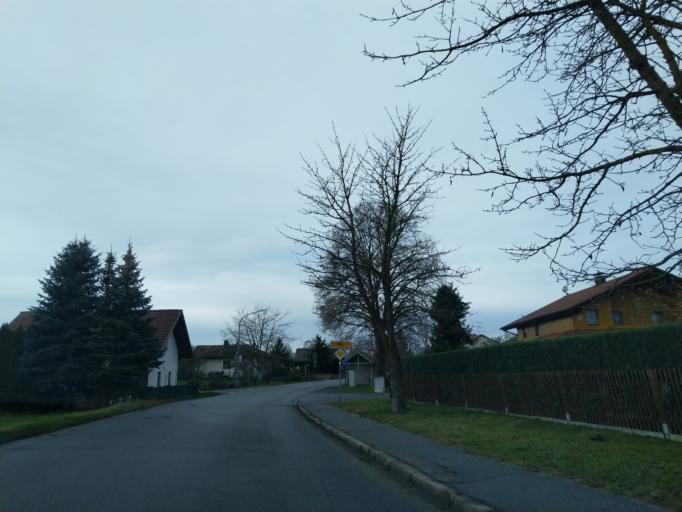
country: DE
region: Bavaria
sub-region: Lower Bavaria
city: Rossbach
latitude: 48.6185
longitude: 12.9836
